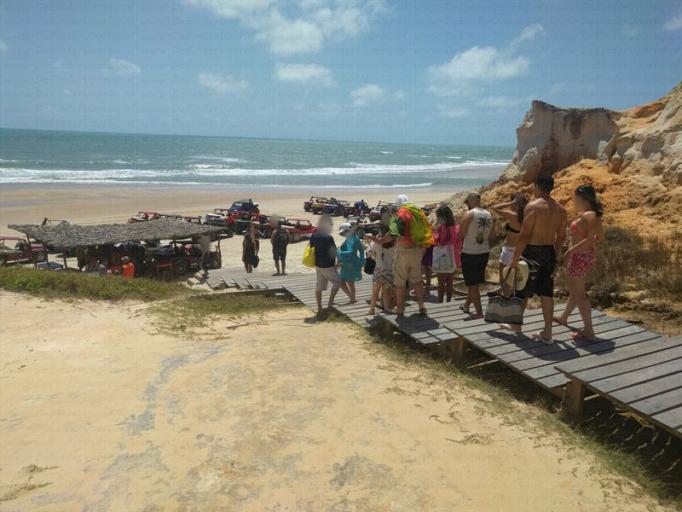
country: BR
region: Ceara
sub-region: Beberibe
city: Beberibe
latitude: -4.1572
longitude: -38.1057
